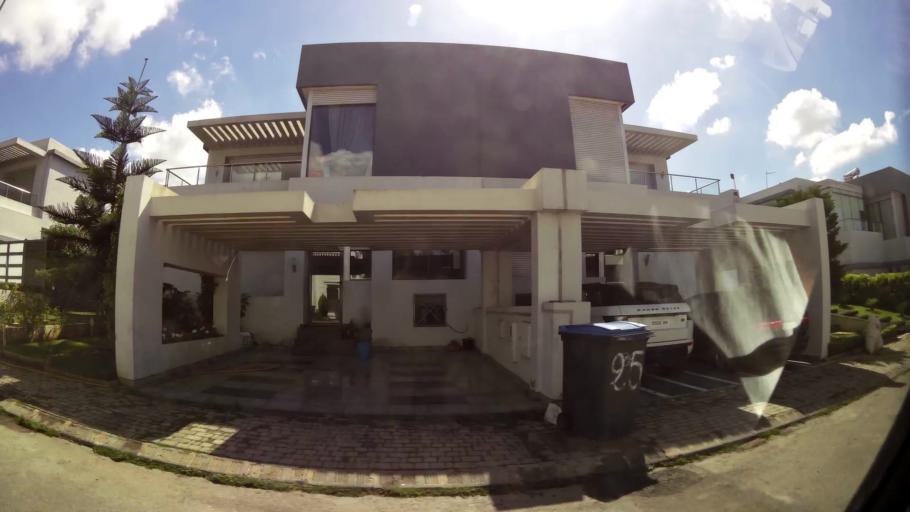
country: MA
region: Grand Casablanca
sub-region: Nouaceur
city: Bouskoura
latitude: 33.4657
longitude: -7.6039
